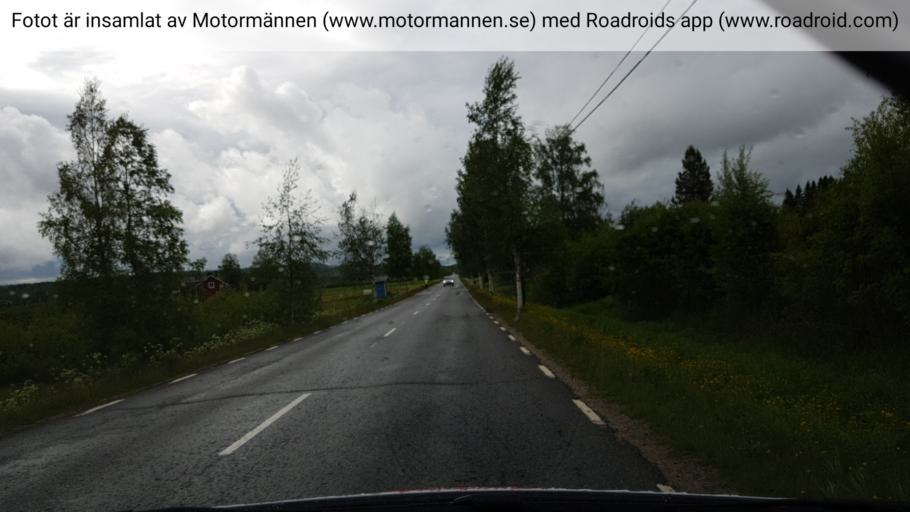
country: SE
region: Vaesterbotten
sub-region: Vannas Kommun
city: Vannasby
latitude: 63.8637
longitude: 19.8996
